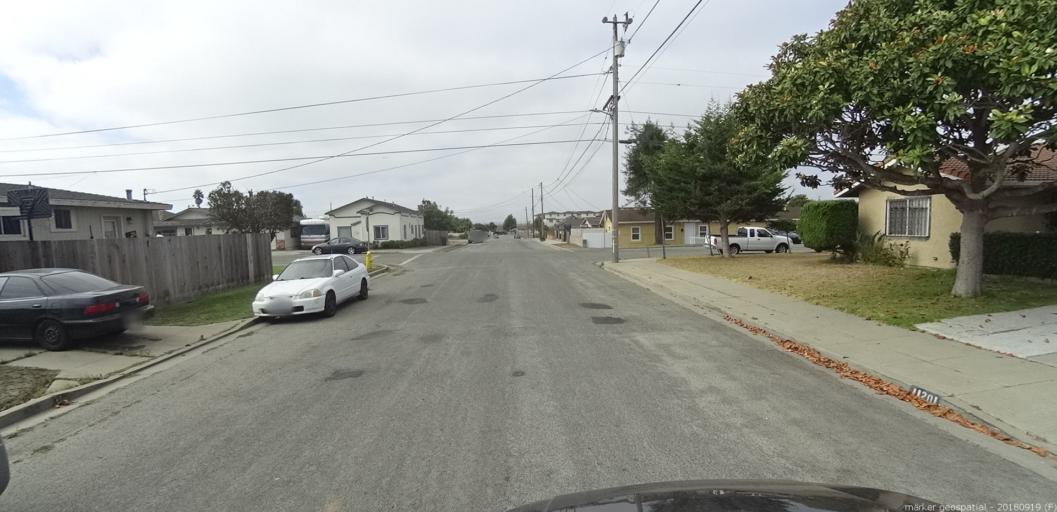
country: US
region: California
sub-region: Monterey County
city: Castroville
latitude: 36.7664
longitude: -121.7545
